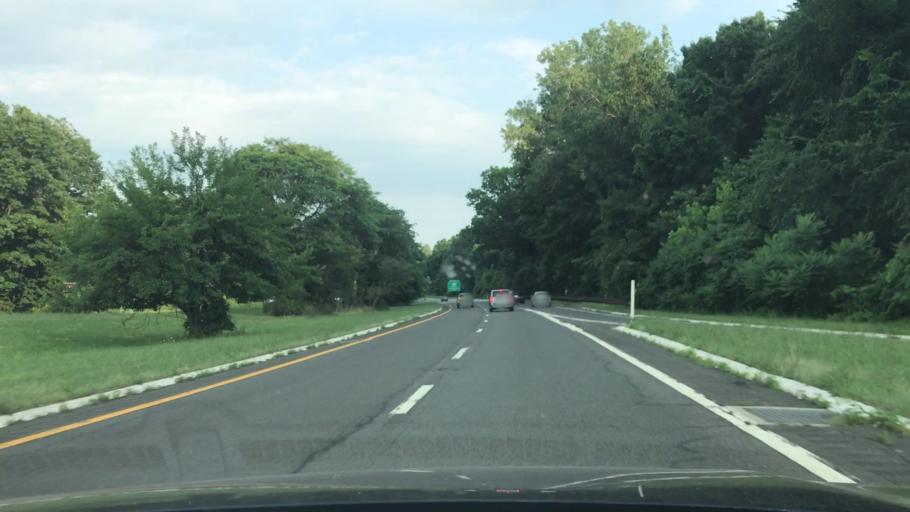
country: US
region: New York
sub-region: Rockland County
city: Orangeburg
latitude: 41.0435
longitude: -73.9575
